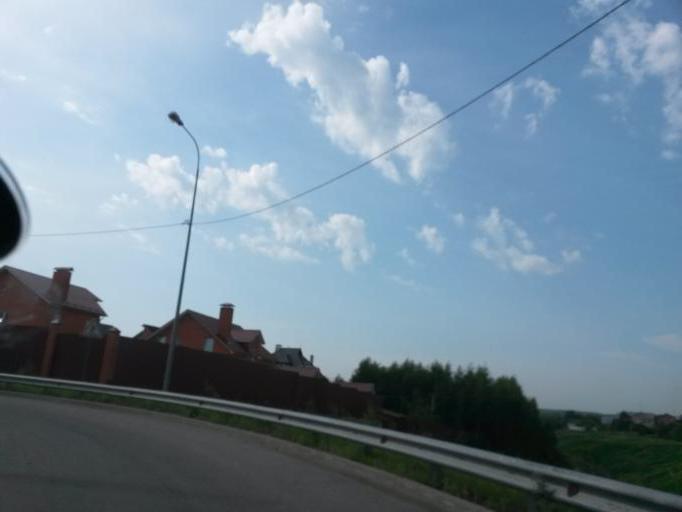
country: RU
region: Moskovskaya
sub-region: Chekhovskiy Rayon
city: Chekhov
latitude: 55.1534
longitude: 37.4565
